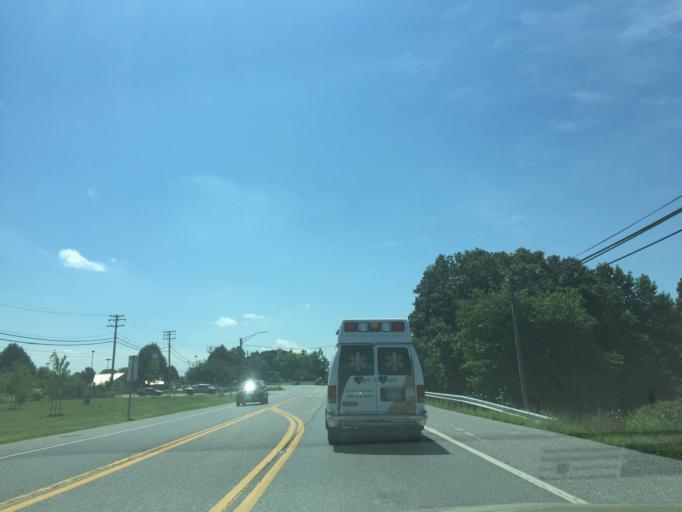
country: US
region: Maryland
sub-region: Harford County
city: Bel Air North
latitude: 39.5771
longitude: -76.3865
